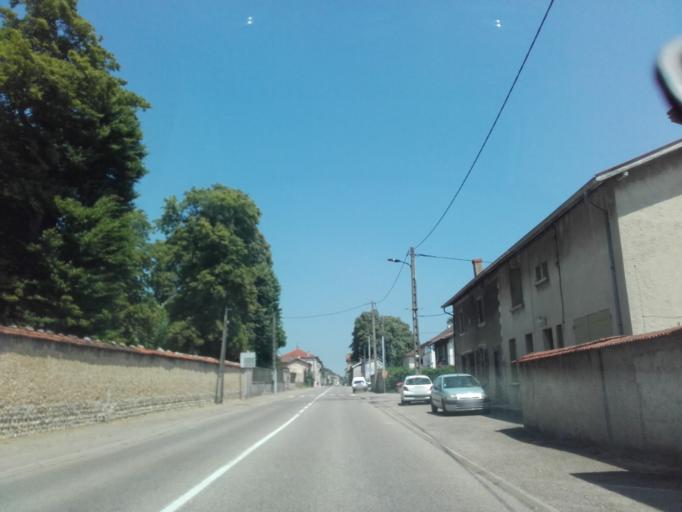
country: FR
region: Rhone-Alpes
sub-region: Departement de l'Isere
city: Champier
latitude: 45.4484
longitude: 5.2896
